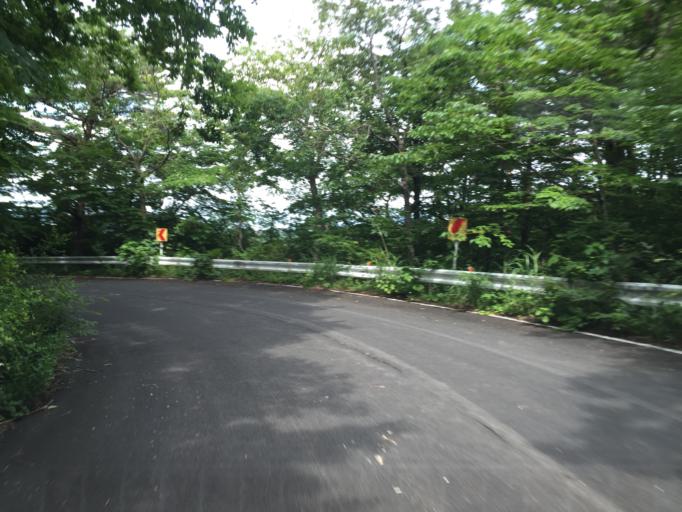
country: JP
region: Fukushima
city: Nihommatsu
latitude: 37.6660
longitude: 140.3329
